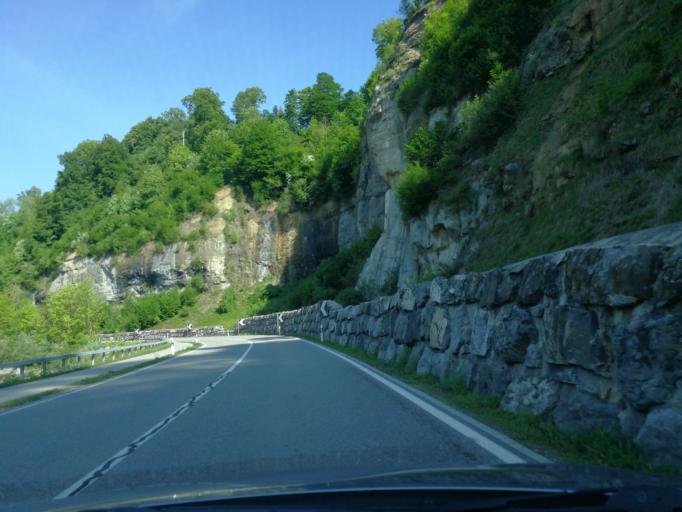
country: CH
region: Lucerne
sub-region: Entlebuch District
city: Werthenstein
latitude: 47.0511
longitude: 8.1135
